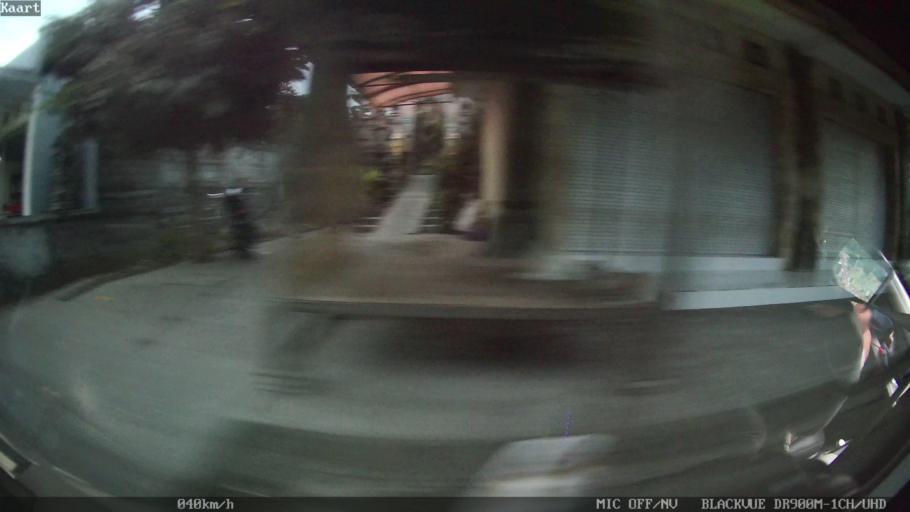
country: ID
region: Bali
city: Banjar Pasekan
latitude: -8.6281
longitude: 115.2923
